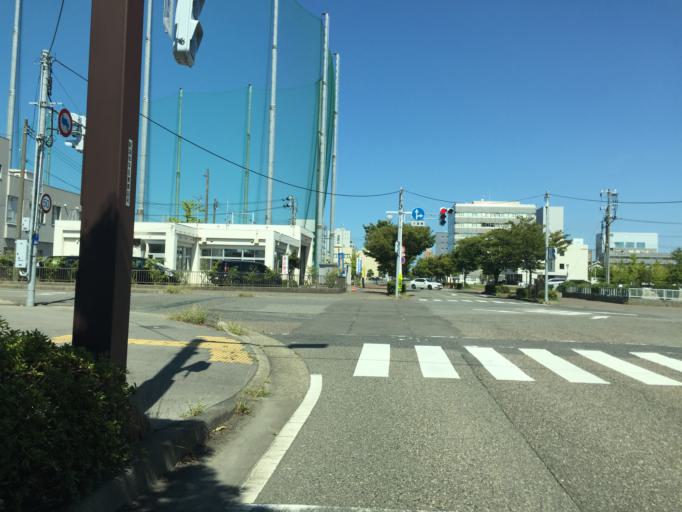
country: JP
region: Niigata
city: Niigata-shi
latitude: 37.8961
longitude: 139.0178
